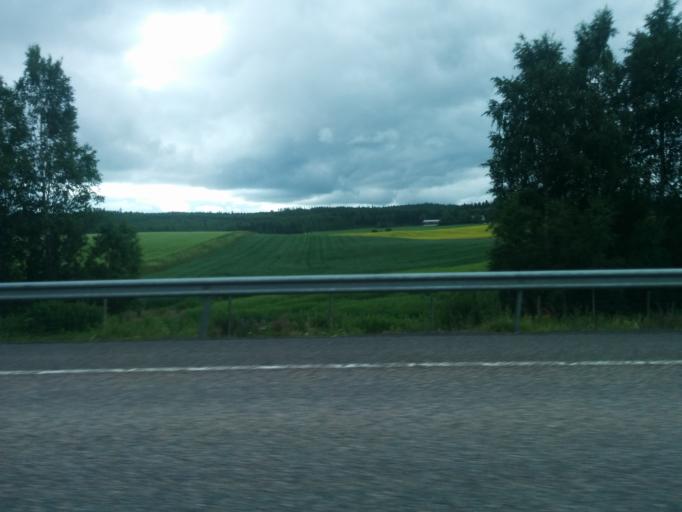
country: FI
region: Pirkanmaa
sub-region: Tampere
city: Orivesi
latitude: 61.7106
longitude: 24.5042
